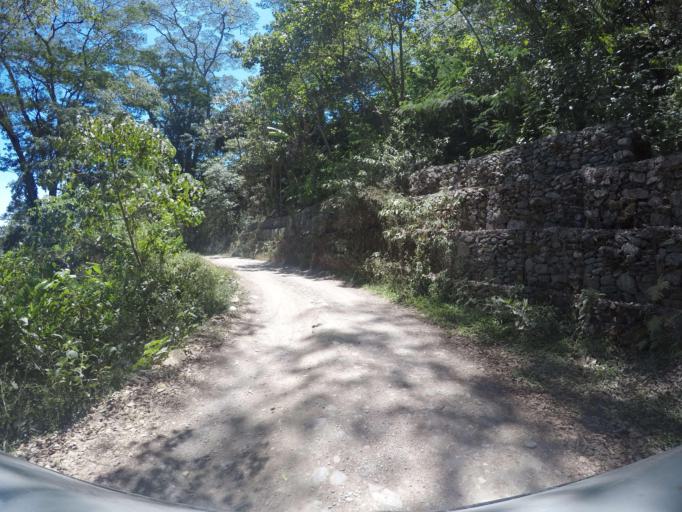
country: TL
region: Ermera
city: Gleno
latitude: -8.7409
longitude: 125.4066
